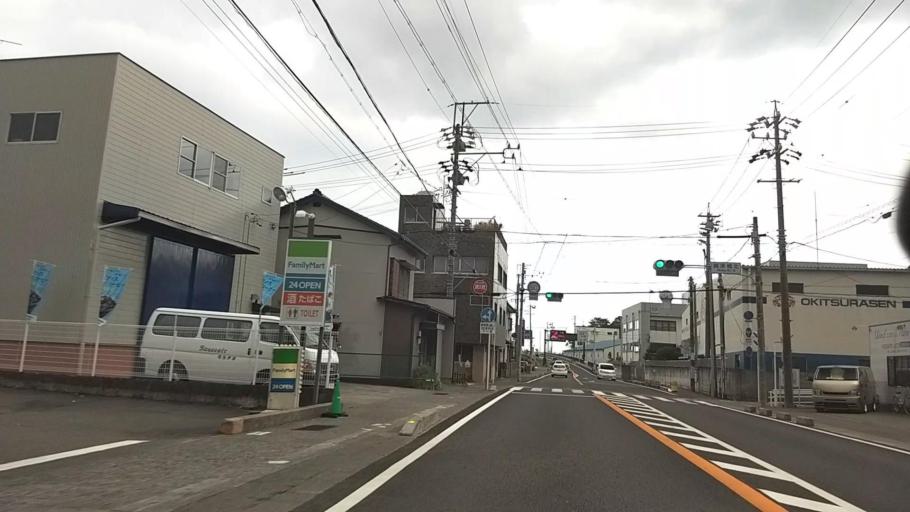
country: JP
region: Shizuoka
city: Shizuoka-shi
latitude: 35.0589
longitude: 138.5260
